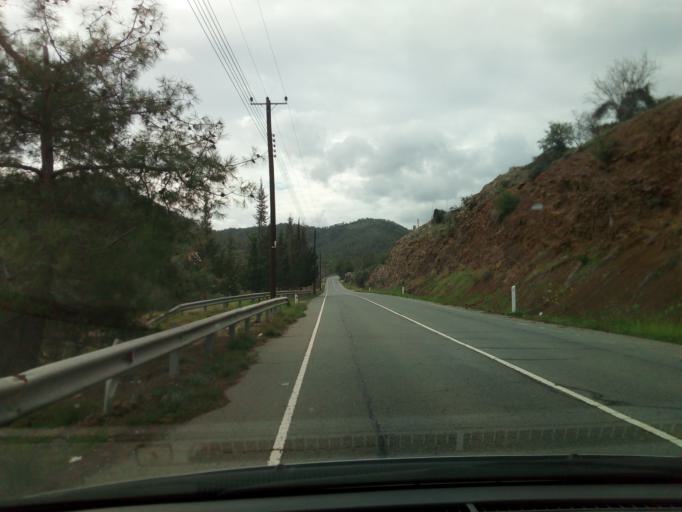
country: CY
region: Lefkosia
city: Klirou
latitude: 35.0036
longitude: 33.1434
